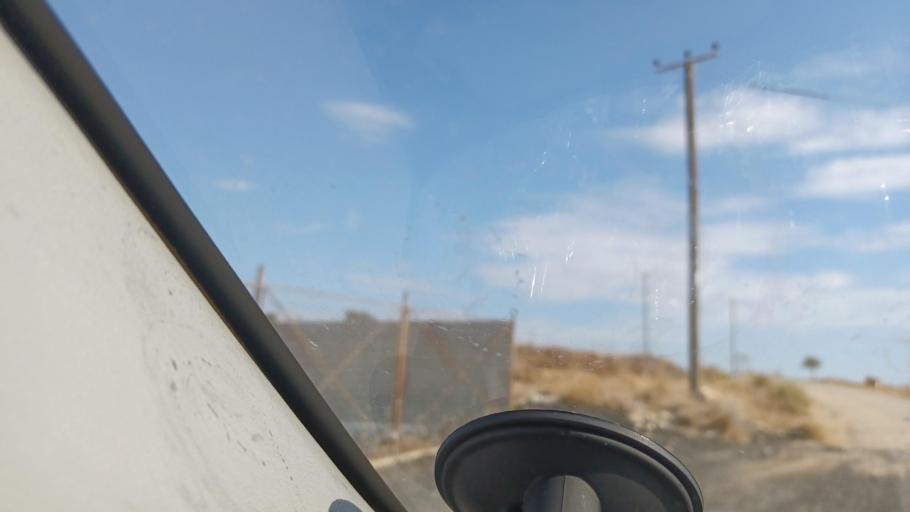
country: CY
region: Pafos
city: Mesogi
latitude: 34.7412
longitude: 32.5469
